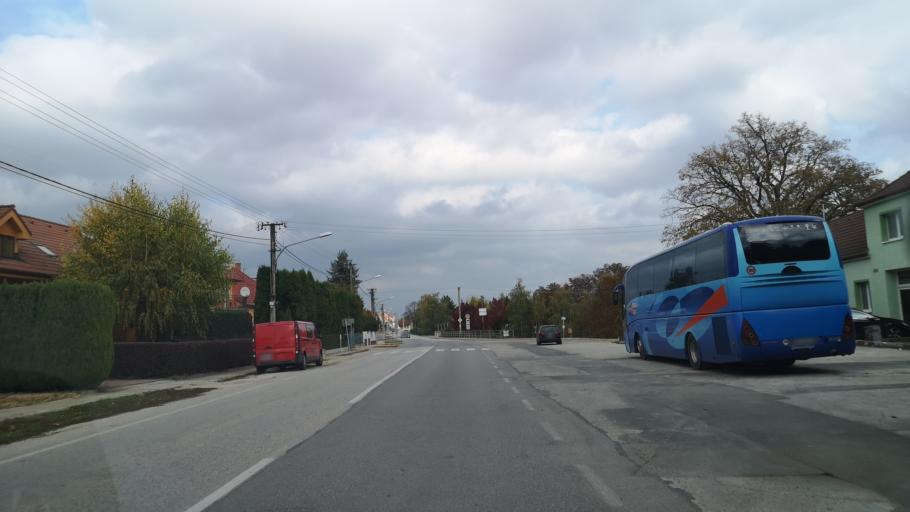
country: SK
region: Nitriansky
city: Cachtice
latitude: 48.6778
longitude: 17.7729
